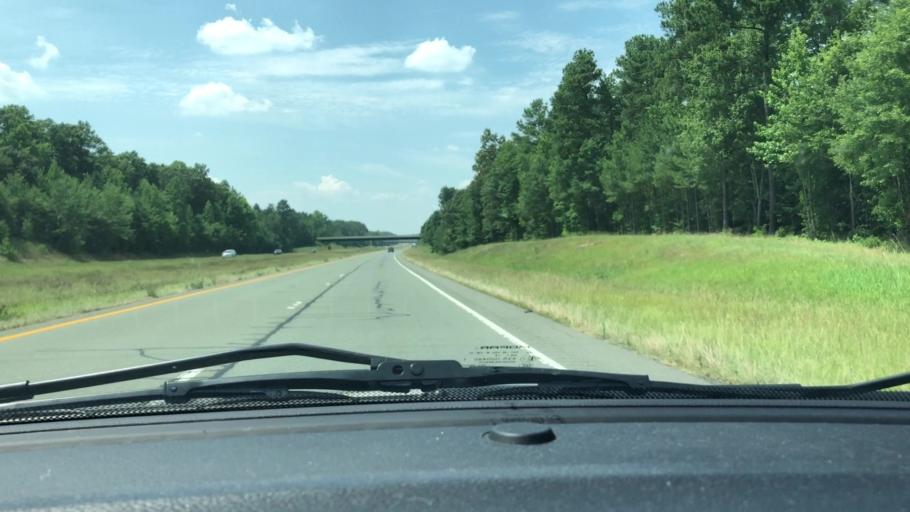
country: US
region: North Carolina
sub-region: Randolph County
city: Liberty
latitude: 35.7945
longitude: -79.5313
